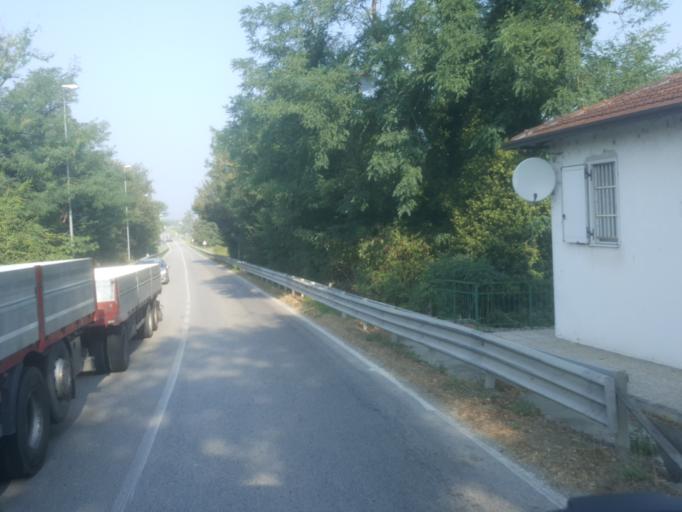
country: IT
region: Emilia-Romagna
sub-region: Provincia di Ravenna
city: Voltana
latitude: 44.5550
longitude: 11.9342
